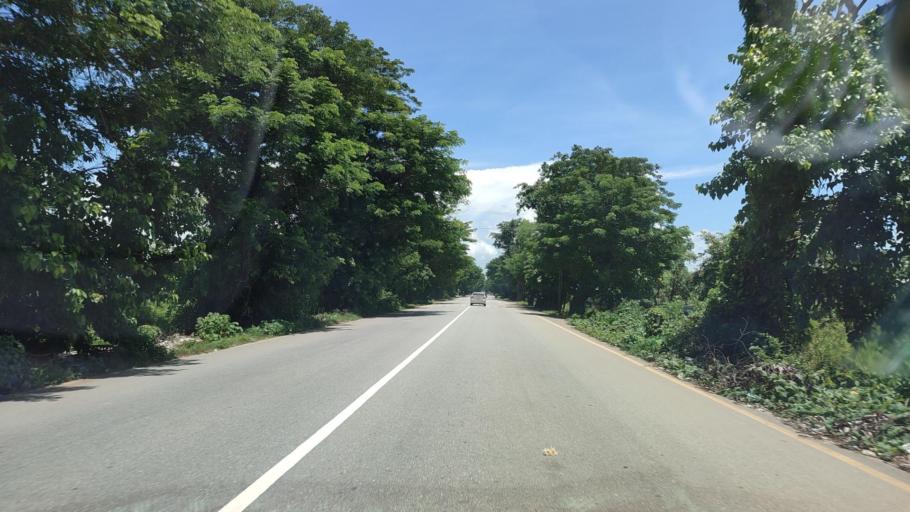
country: MM
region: Bago
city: Pyu
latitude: 18.2688
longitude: 96.5251
